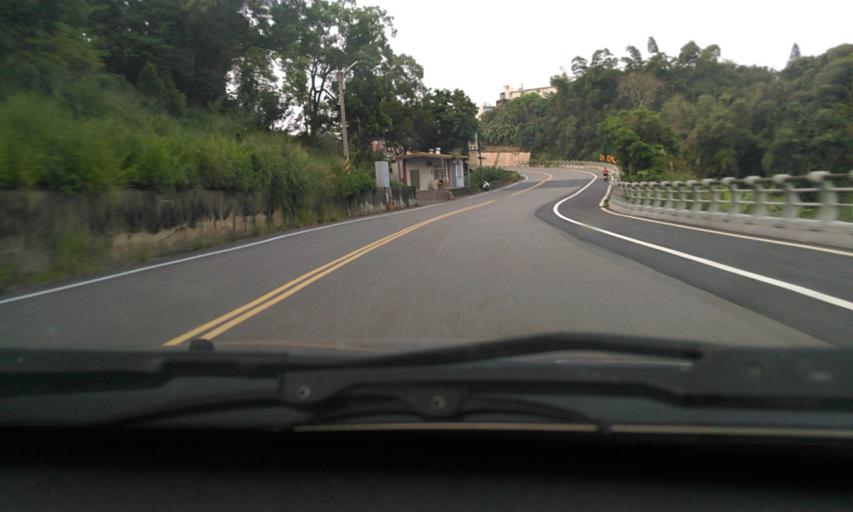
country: TW
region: Taiwan
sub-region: Hsinchu
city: Hsinchu
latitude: 24.6852
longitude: 120.9861
